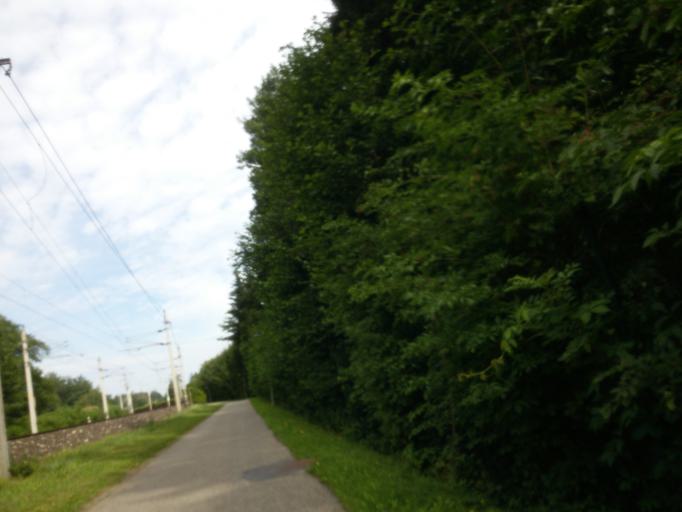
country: AT
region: Carinthia
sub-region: Politischer Bezirk Klagenfurt Land
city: Keutschach am See
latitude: 46.6205
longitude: 14.1972
